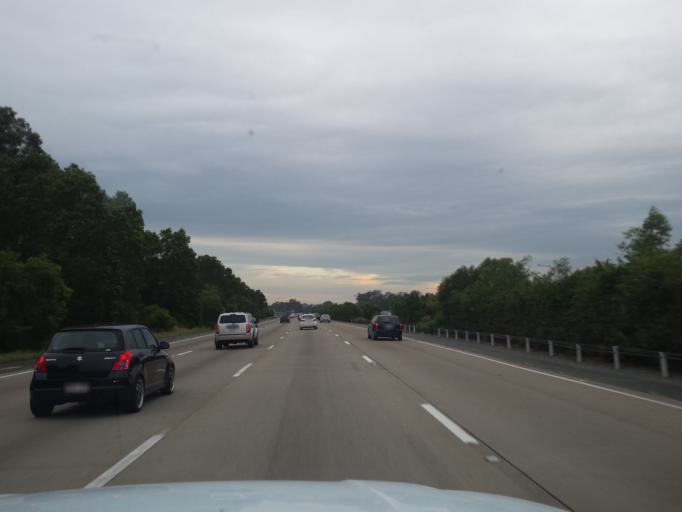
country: AU
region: Queensland
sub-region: Gold Coast
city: Oxenford
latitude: -27.8600
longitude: 153.3099
